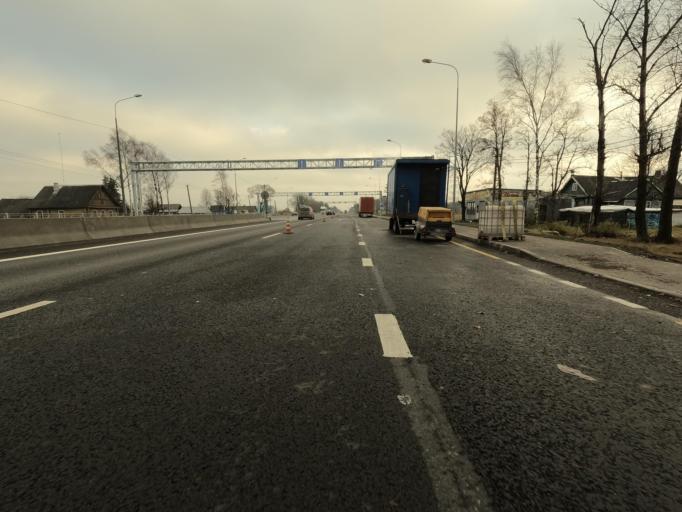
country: RU
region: Leningrad
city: Mga
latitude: 59.7259
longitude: 31.0947
